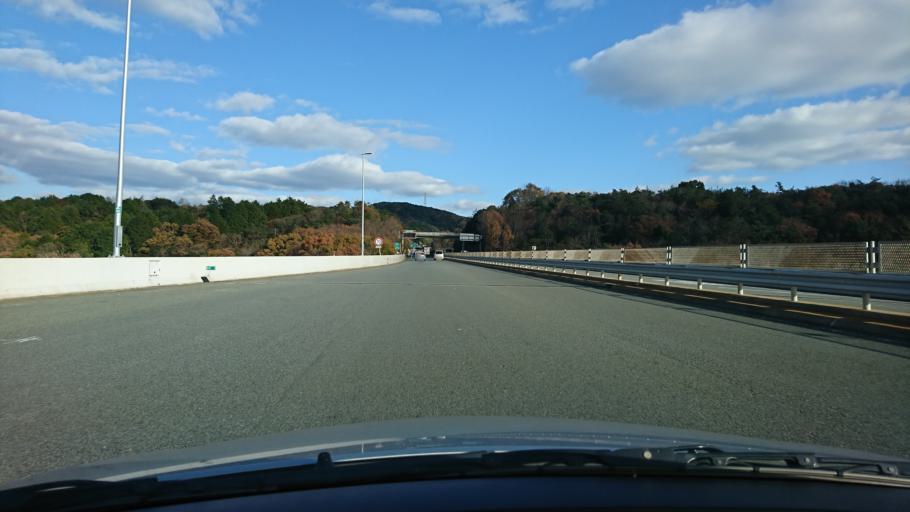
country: JP
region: Hyogo
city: Akashi
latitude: 34.6997
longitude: 135.0598
